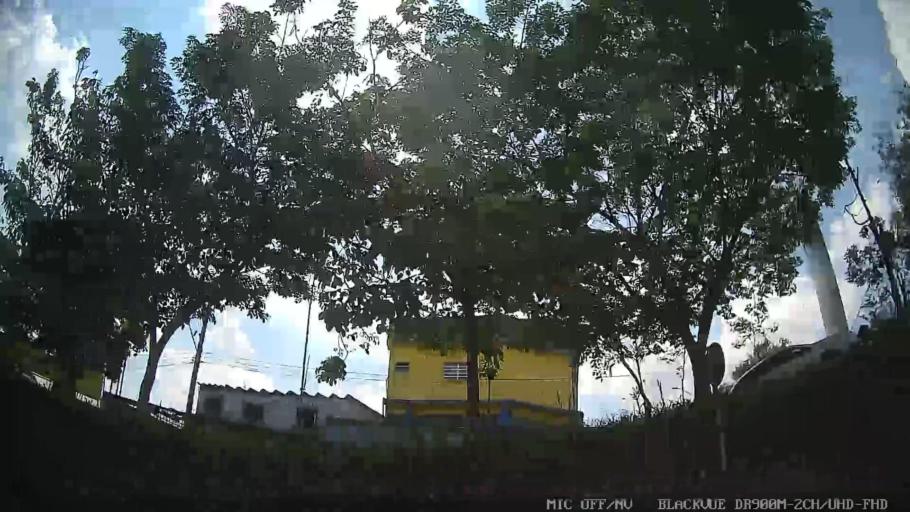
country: BR
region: Sao Paulo
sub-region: Taboao Da Serra
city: Taboao da Serra
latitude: -23.6763
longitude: -46.7922
